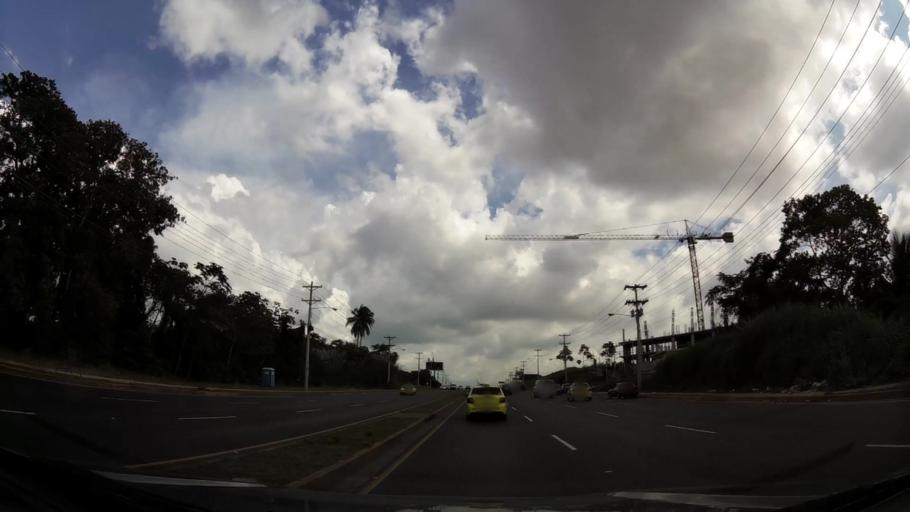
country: PA
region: Panama
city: San Miguelito
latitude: 9.0558
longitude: -79.4369
